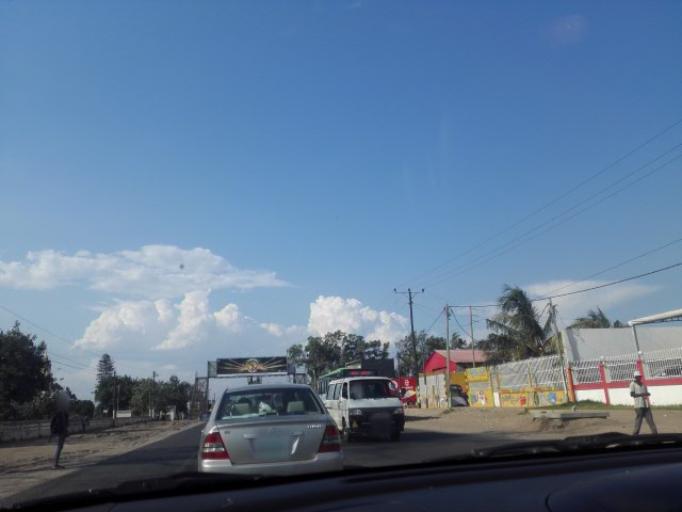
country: MZ
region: Maputo City
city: Maputo
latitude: -25.8606
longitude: 32.5667
